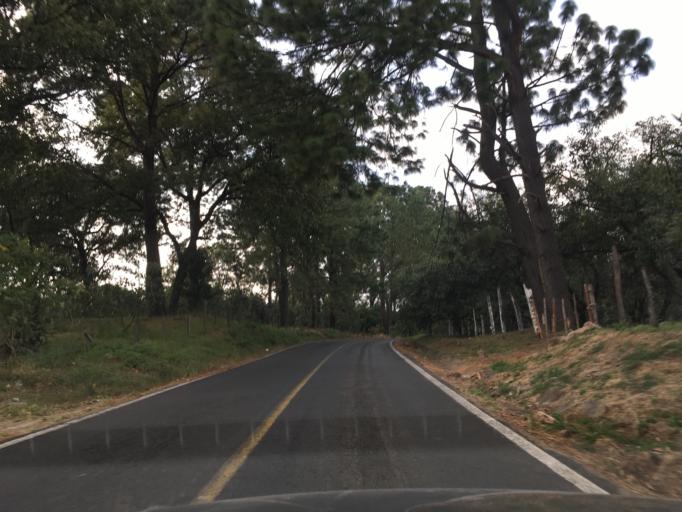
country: MX
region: Michoacan
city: Tingambato
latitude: 19.4665
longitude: -101.8901
